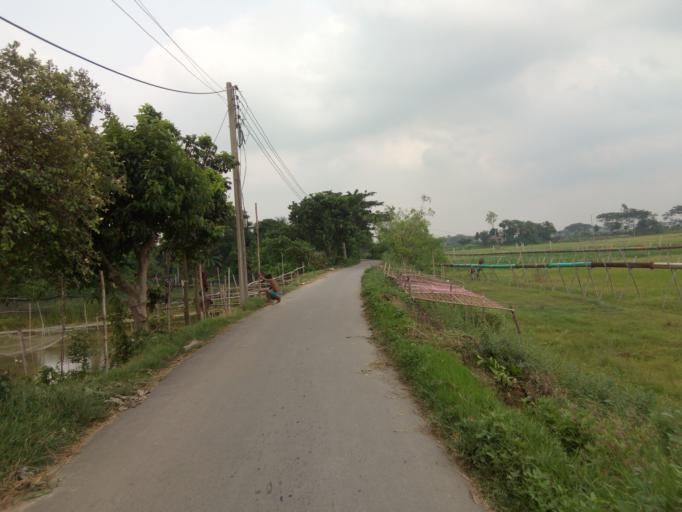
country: BD
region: Dhaka
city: Paltan
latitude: 23.7467
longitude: 90.4772
